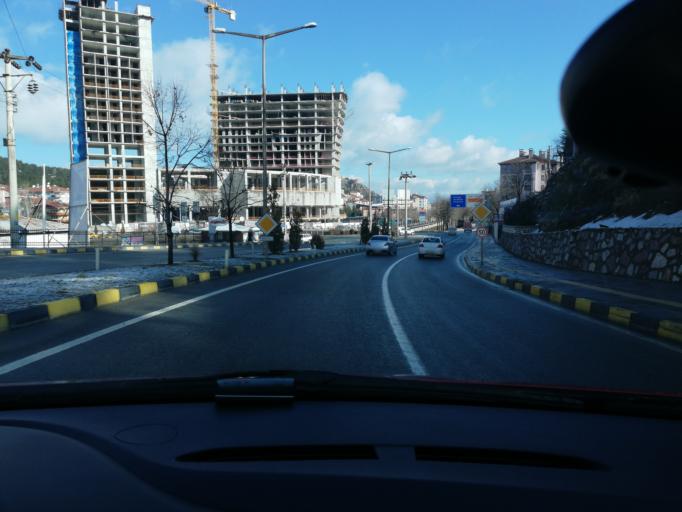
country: TR
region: Kastamonu
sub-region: Cide
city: Kastamonu
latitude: 41.3620
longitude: 33.7666
